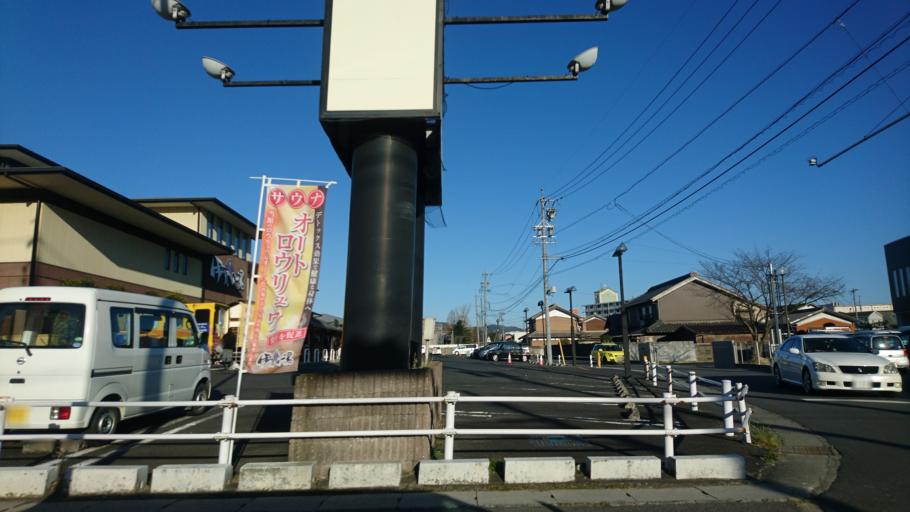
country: JP
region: Mie
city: Ueno-ebisumachi
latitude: 34.7547
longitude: 136.1329
